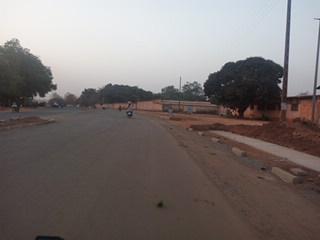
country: BJ
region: Borgou
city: Parakou
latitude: 9.3412
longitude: 2.6059
